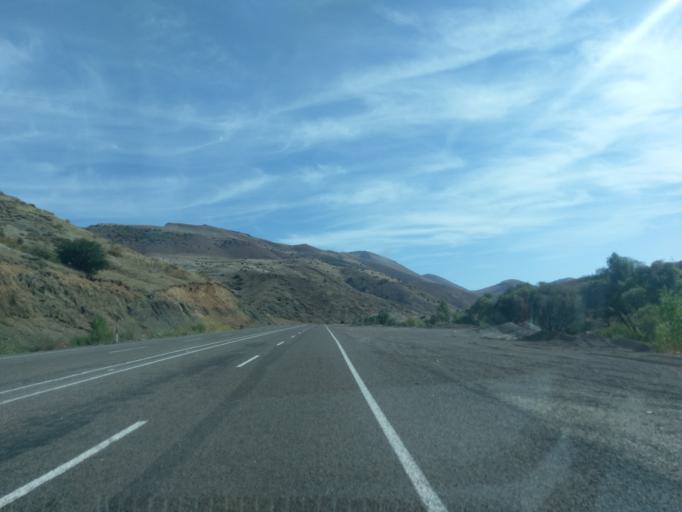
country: TR
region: Sivas
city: Imranli
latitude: 39.8614
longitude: 38.3261
